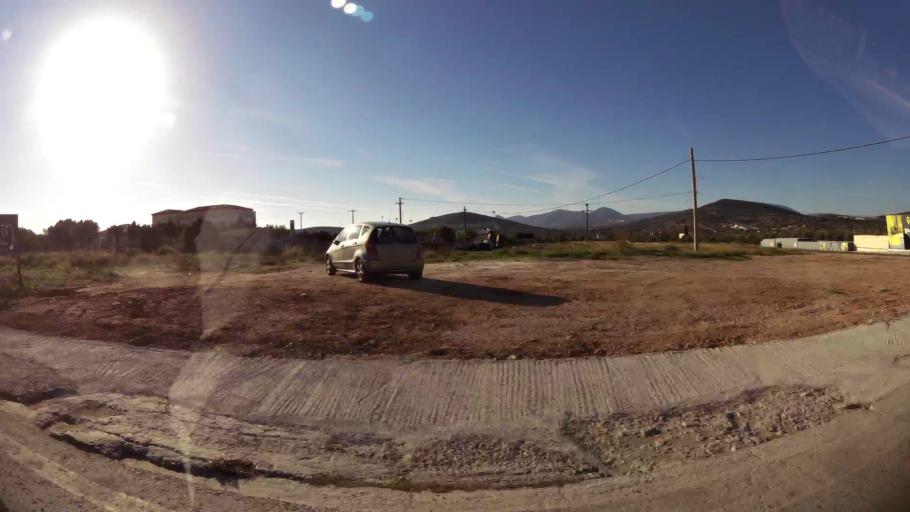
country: GR
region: Attica
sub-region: Nomarchia Anatolikis Attikis
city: Kalyvia Thorikou
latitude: 37.8440
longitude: 23.9241
